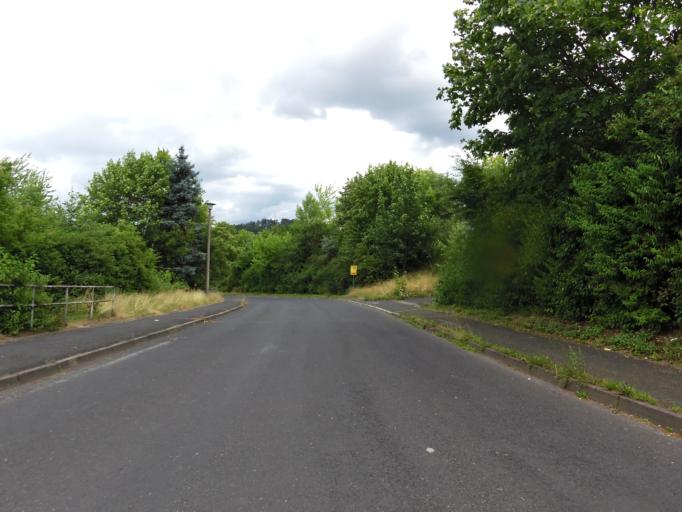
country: DE
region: Thuringia
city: Bad Salzungen
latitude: 50.8090
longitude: 10.2511
